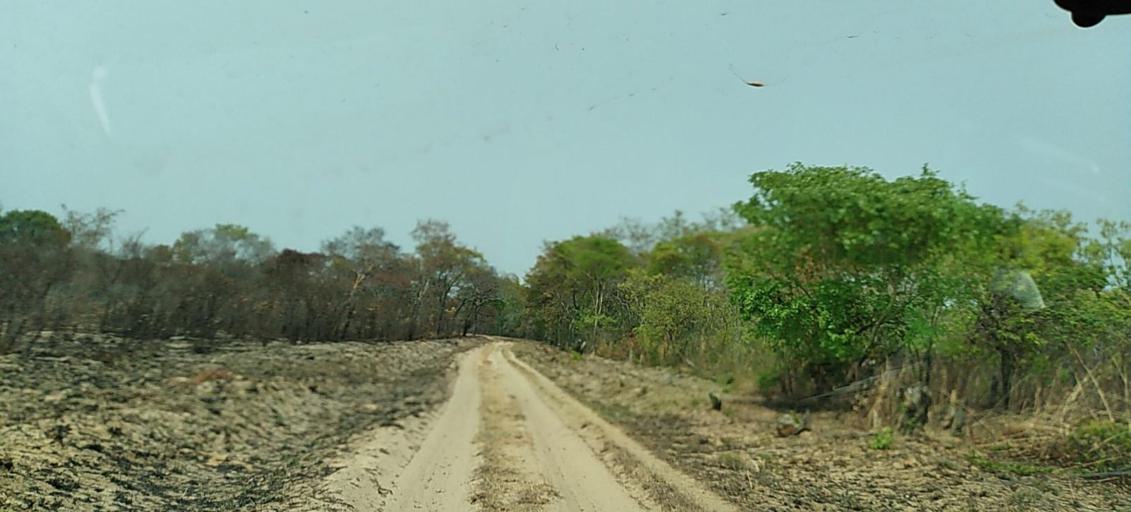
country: ZM
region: North-Western
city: Zambezi
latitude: -13.9354
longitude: 23.2230
